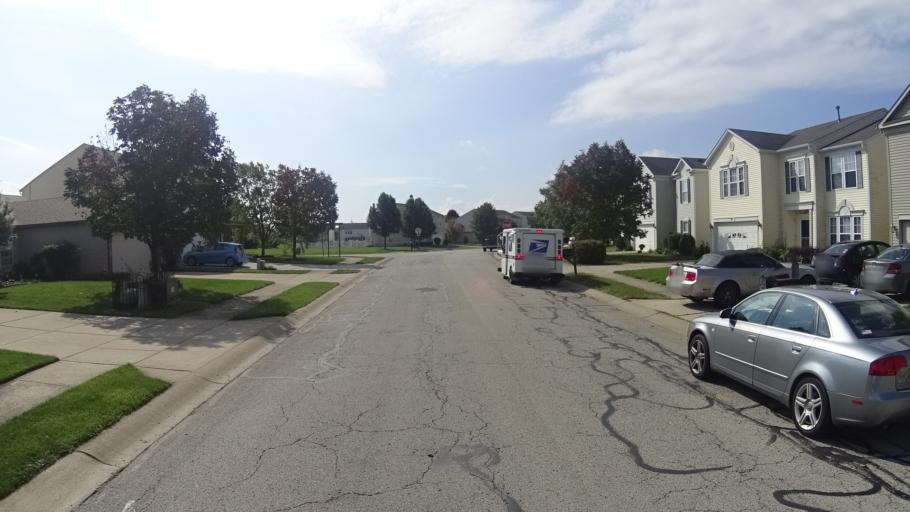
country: US
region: Indiana
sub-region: Madison County
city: Ingalls
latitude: 39.9838
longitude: -85.8481
